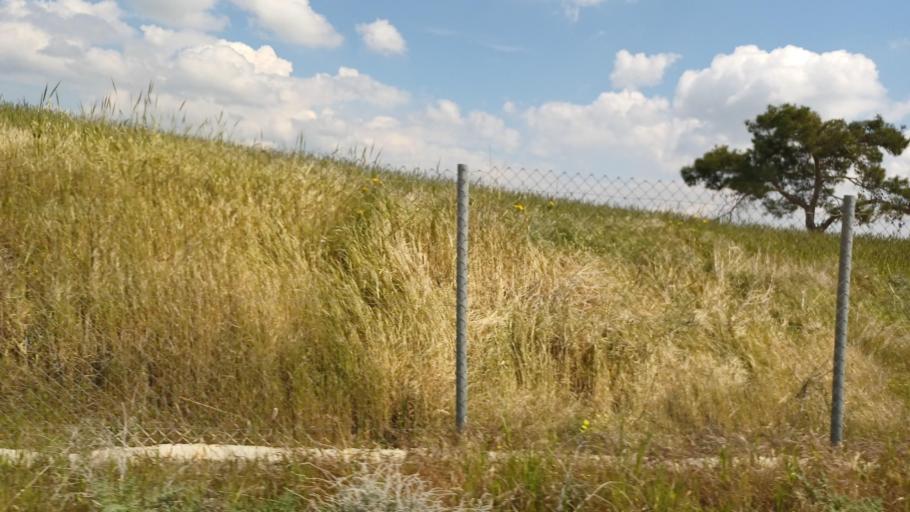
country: CY
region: Lefkosia
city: Kakopetria
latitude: 35.0775
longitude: 32.9427
